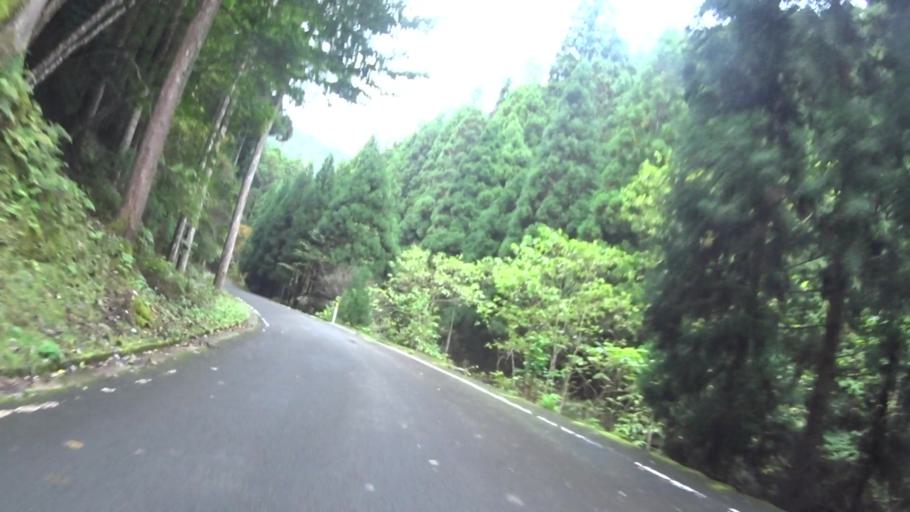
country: JP
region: Fukui
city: Obama
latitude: 35.2748
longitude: 135.7083
